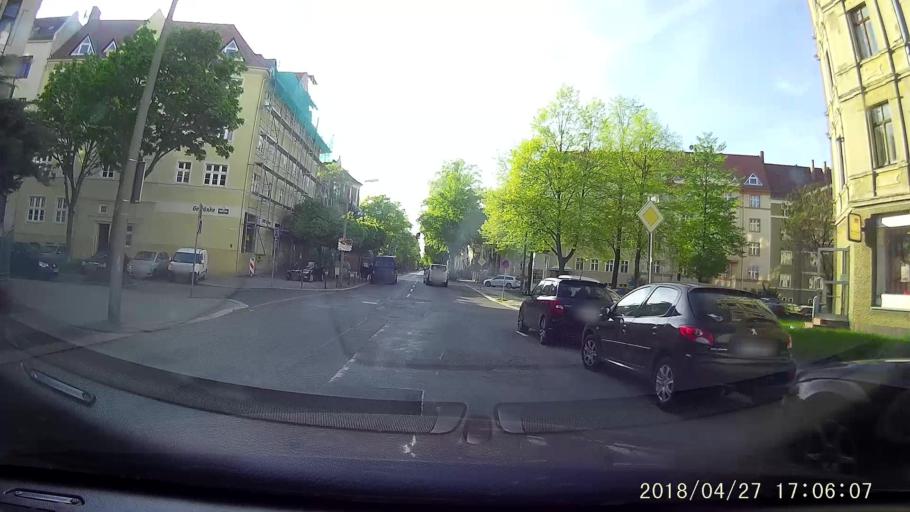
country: DE
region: Saxony
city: Goerlitz
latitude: 51.1441
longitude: 14.9683
